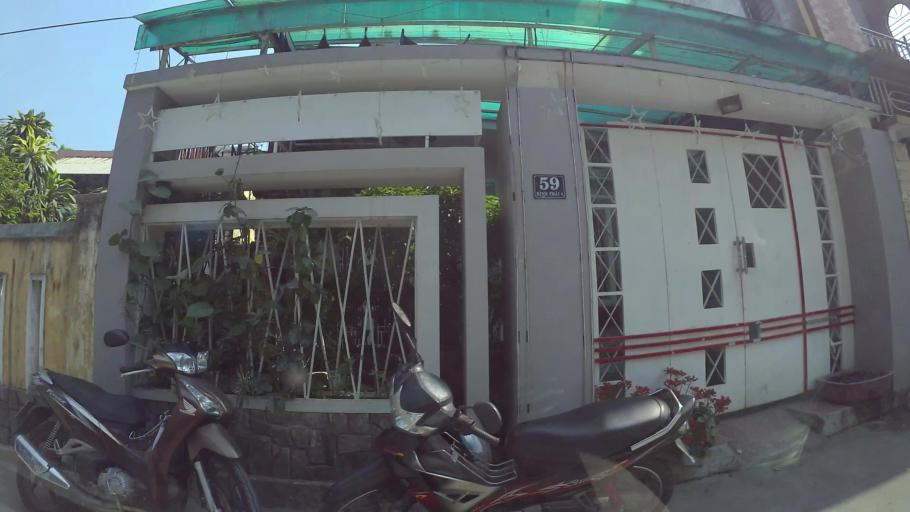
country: VN
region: Da Nang
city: Cam Le
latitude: 16.0126
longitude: 108.2018
